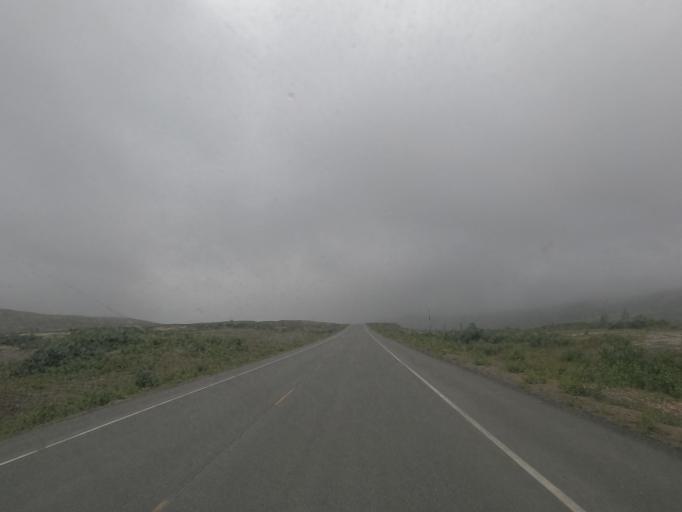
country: US
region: Alaska
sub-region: Haines Borough
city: Haines
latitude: 59.6813
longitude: -136.5748
